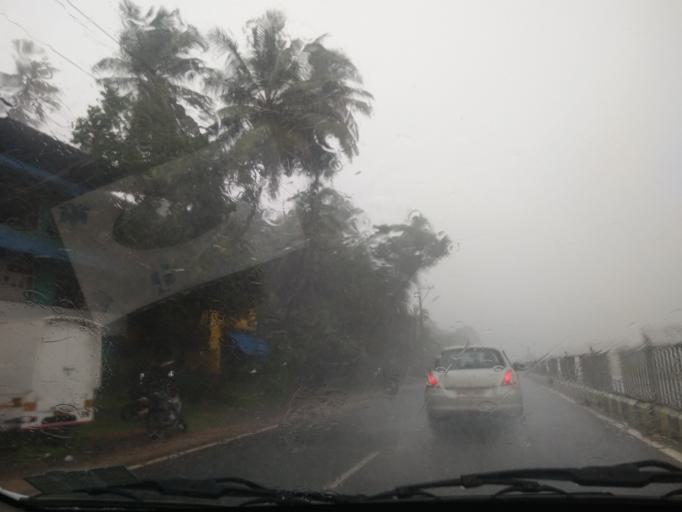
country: IN
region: Goa
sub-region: North Goa
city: Bambolim
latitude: 15.4759
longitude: 73.8493
